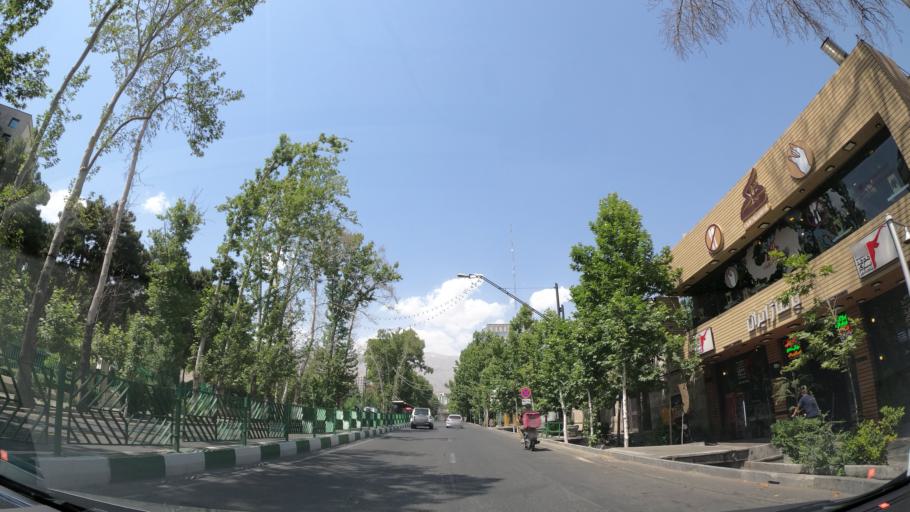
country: IR
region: Tehran
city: Tajrish
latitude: 35.7872
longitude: 51.4155
